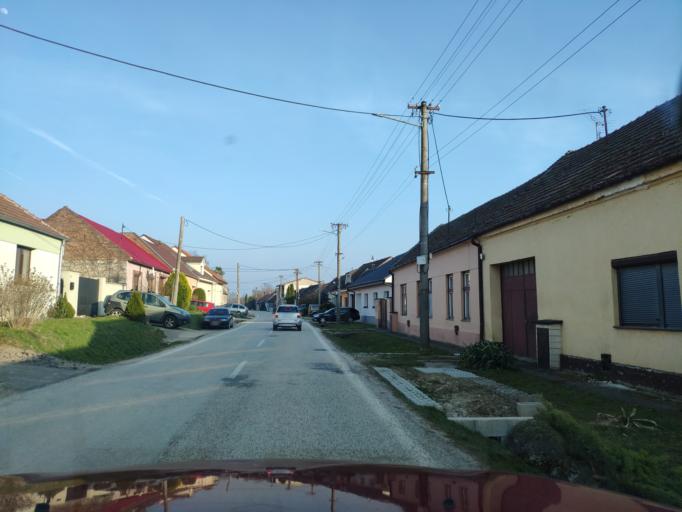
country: SK
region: Bratislavsky
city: Modra
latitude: 48.3321
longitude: 17.4030
